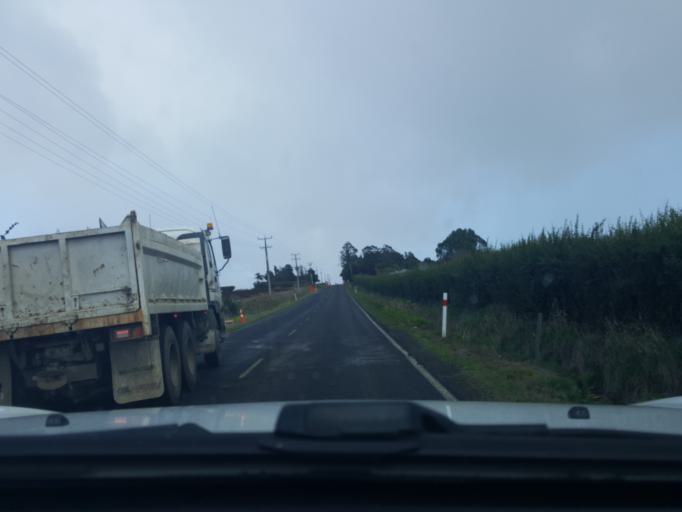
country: NZ
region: Auckland
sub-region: Auckland
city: Pukekohe East
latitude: -37.3084
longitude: 174.9946
